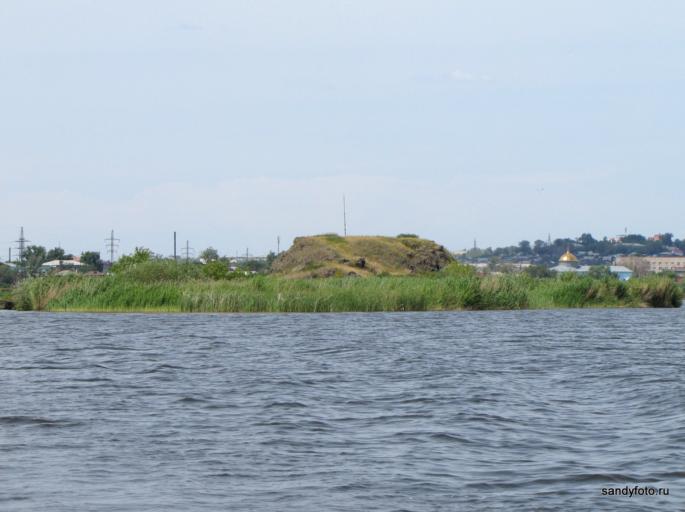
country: RU
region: Chelyabinsk
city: Troitsk
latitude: 54.0741
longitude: 61.5778
